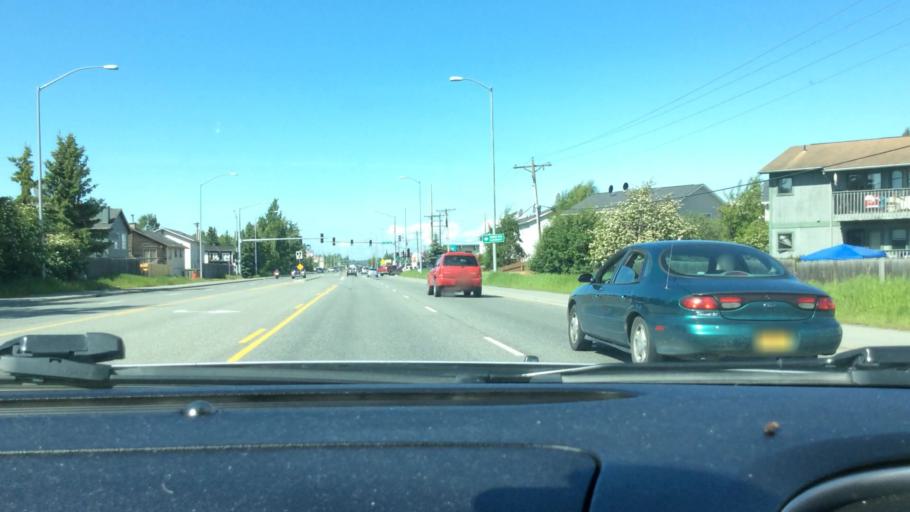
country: US
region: Alaska
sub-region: Anchorage Municipality
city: Anchorage
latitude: 61.2172
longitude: -149.7784
